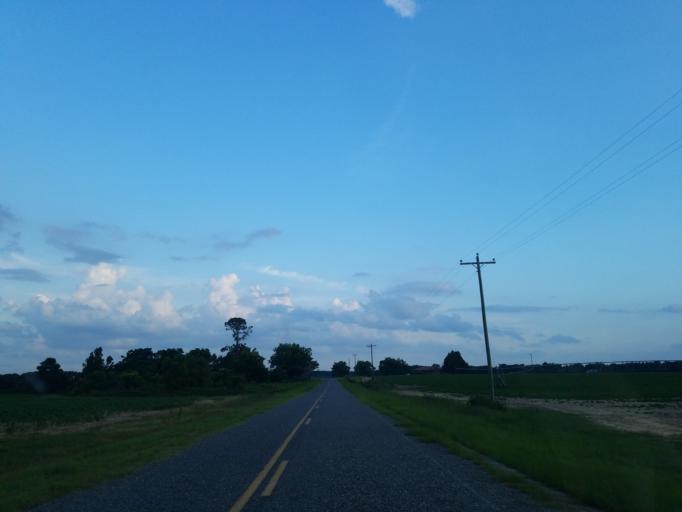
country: US
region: Georgia
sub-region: Dooly County
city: Unadilla
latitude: 32.1647
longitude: -83.7210
